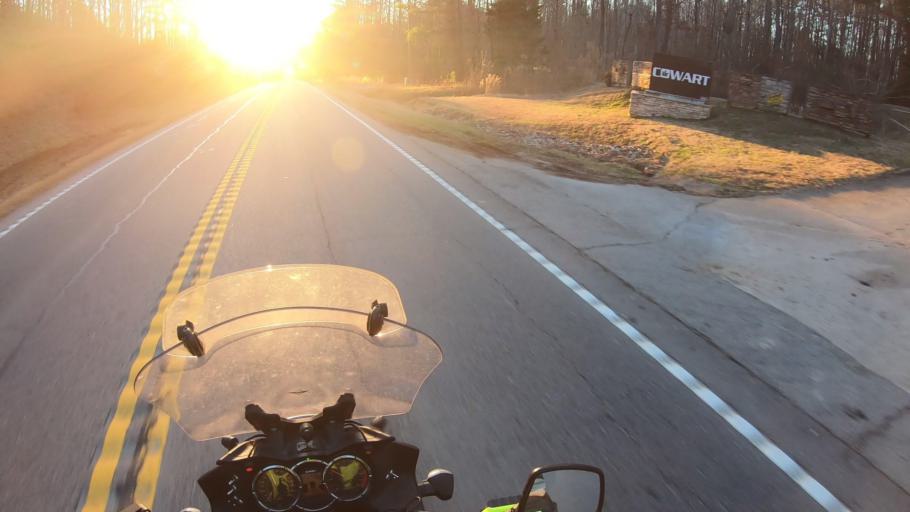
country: US
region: Georgia
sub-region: Cherokee County
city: Ball Ground
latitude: 34.2955
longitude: -84.2581
